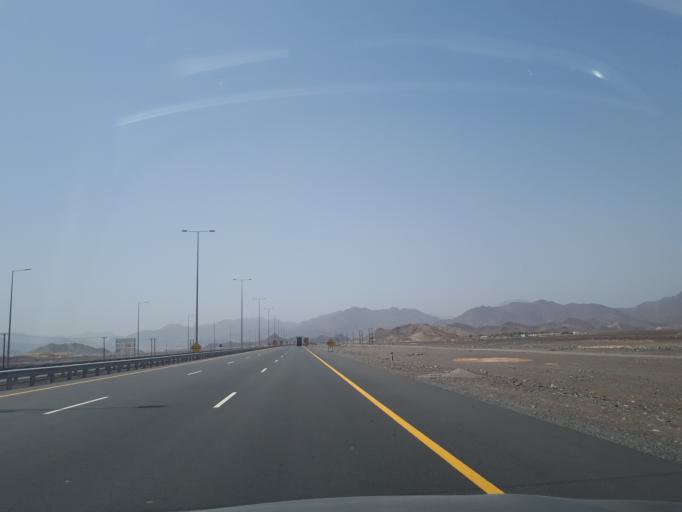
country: OM
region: Muhafazat ad Dakhiliyah
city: Sufalat Sama'il
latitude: 23.3015
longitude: 58.1106
